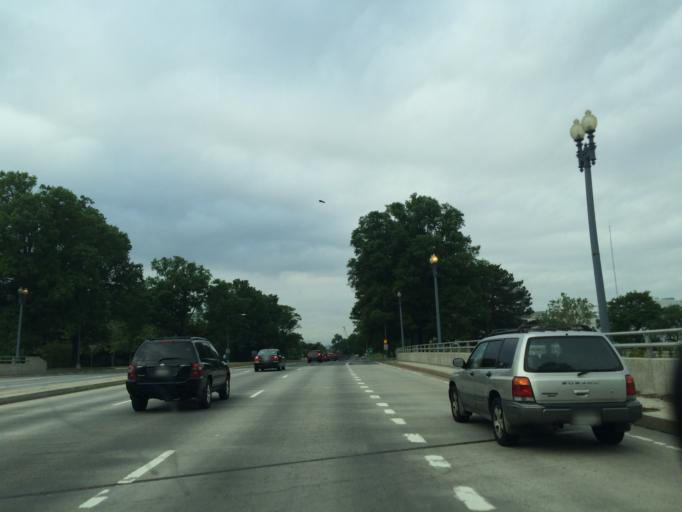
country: US
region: Maryland
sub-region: Prince George's County
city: Chillum
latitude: 38.9317
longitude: -77.0069
